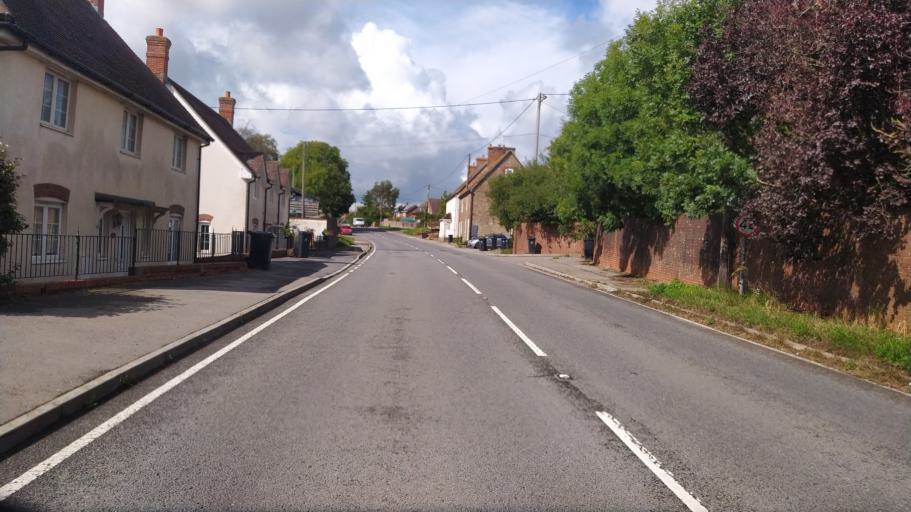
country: GB
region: England
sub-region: Dorset
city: Stalbridge
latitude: 50.9224
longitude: -2.3616
